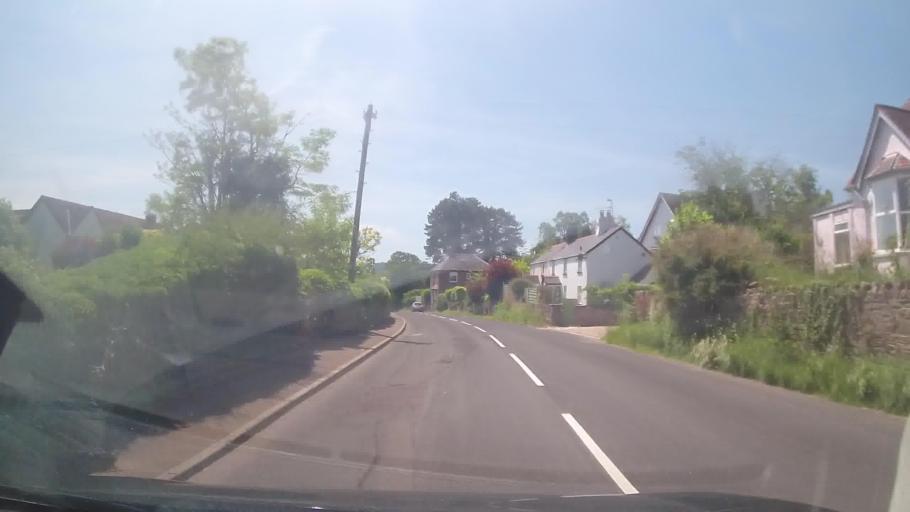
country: GB
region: Wales
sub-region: Monmouthshire
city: Monmouth
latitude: 51.8265
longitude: -2.7126
